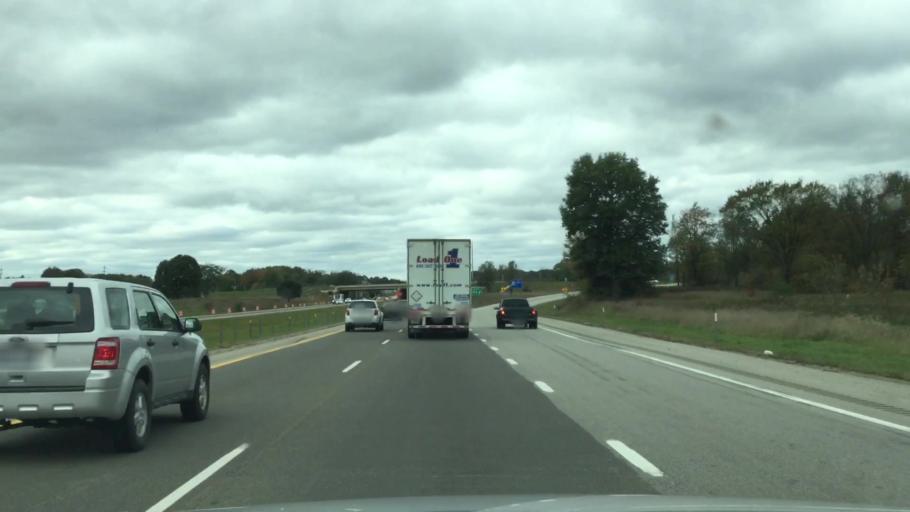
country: US
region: Michigan
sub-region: Calhoun County
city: Springfield
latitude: 42.2711
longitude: -85.2906
